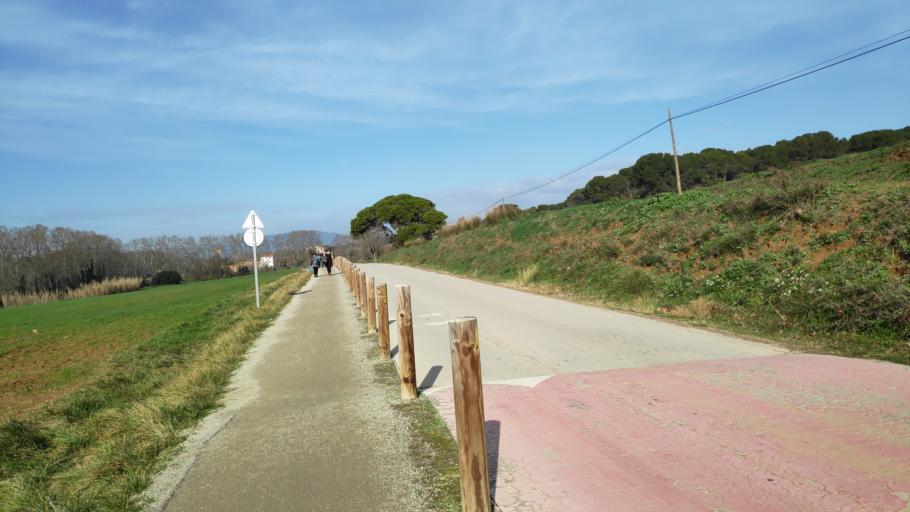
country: ES
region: Catalonia
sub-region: Provincia de Barcelona
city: Mollet del Valles
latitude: 41.5566
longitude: 2.2037
